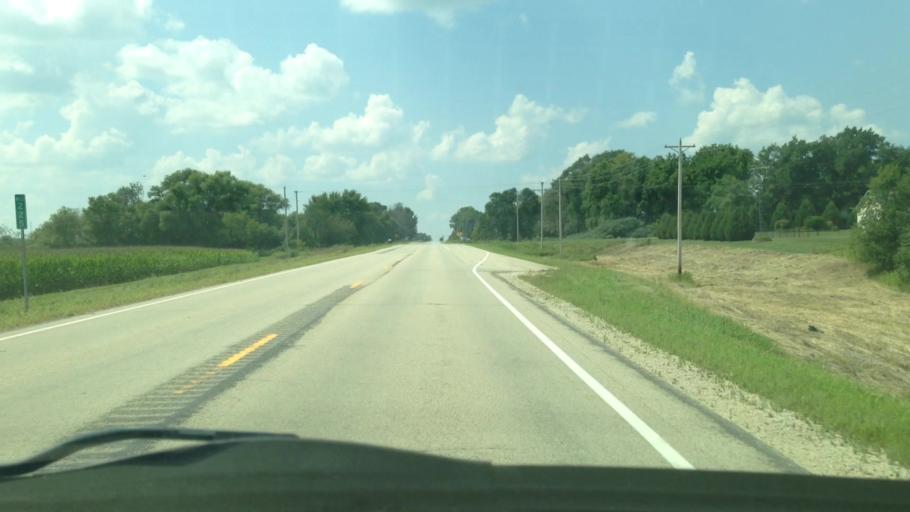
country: US
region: Minnesota
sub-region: Olmsted County
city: Stewartville
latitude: 43.8556
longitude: -92.4660
